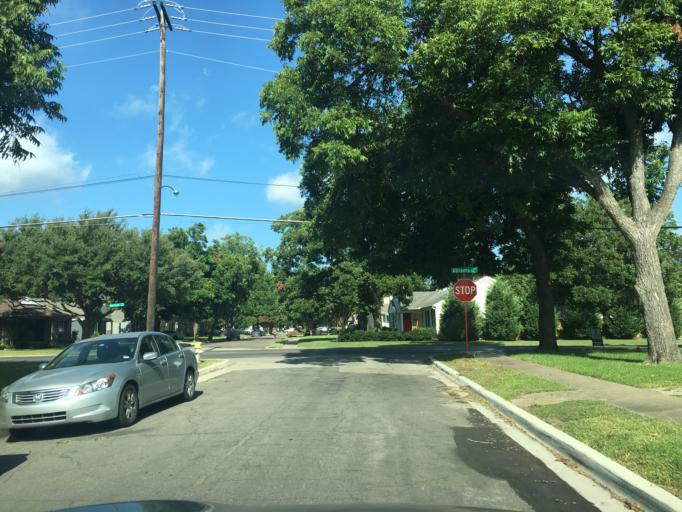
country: US
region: Texas
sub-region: Dallas County
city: Highland Park
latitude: 32.8347
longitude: -96.7525
